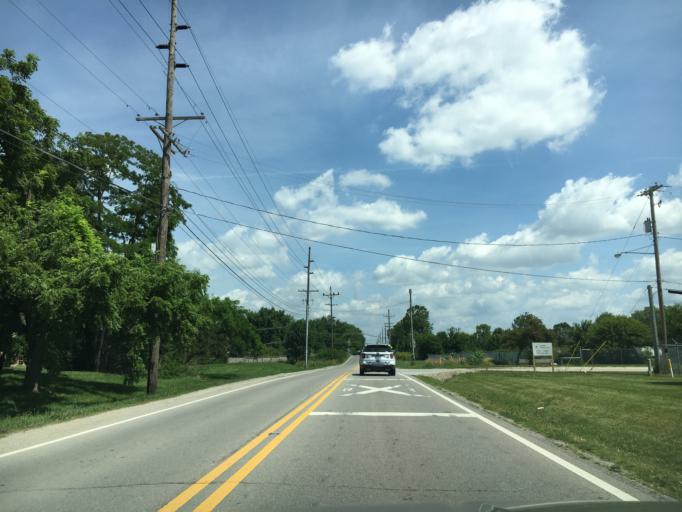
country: US
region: Ohio
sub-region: Franklin County
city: Lincoln Village
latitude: 39.9231
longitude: -83.1441
